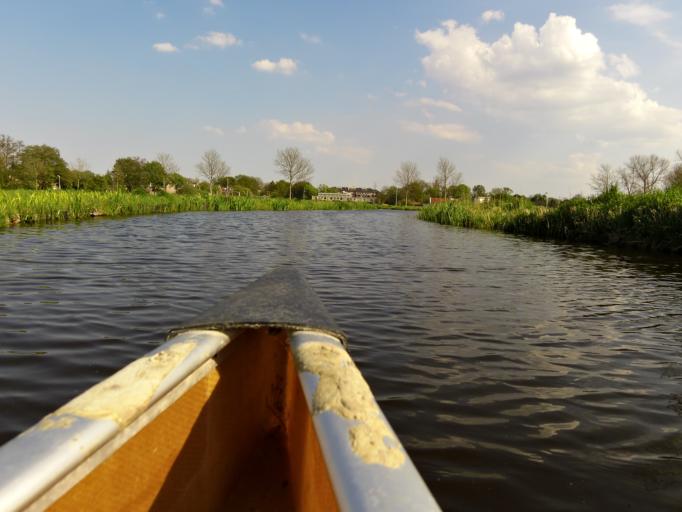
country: NL
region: South Holland
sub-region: Gemeente Voorschoten
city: Voorschoten
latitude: 52.1336
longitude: 4.4426
